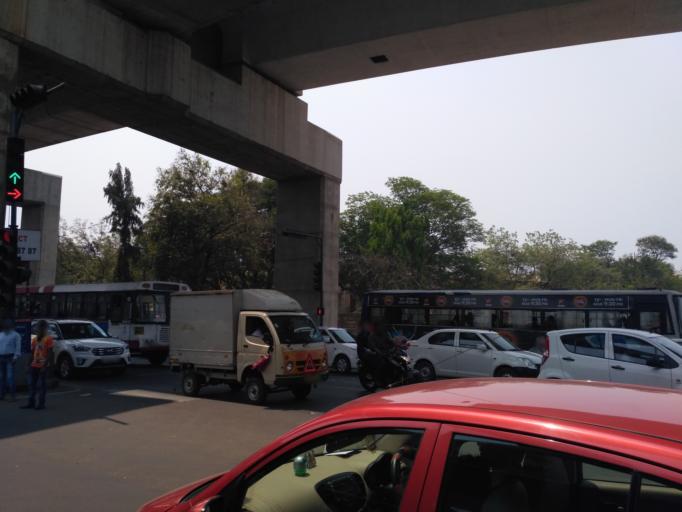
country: IN
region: Telangana
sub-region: Hyderabad
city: Hyderabad
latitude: 17.4369
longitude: 78.4439
